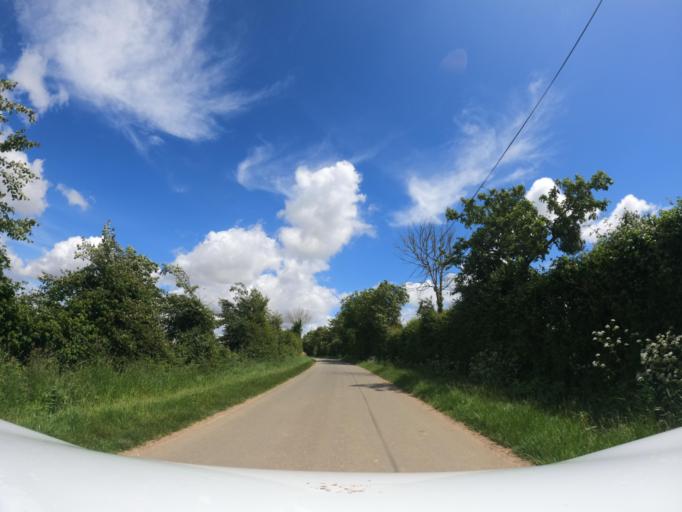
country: FR
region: Pays de la Loire
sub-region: Departement de la Vendee
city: Le Champ-Saint-Pere
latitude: 46.4762
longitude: -1.3108
